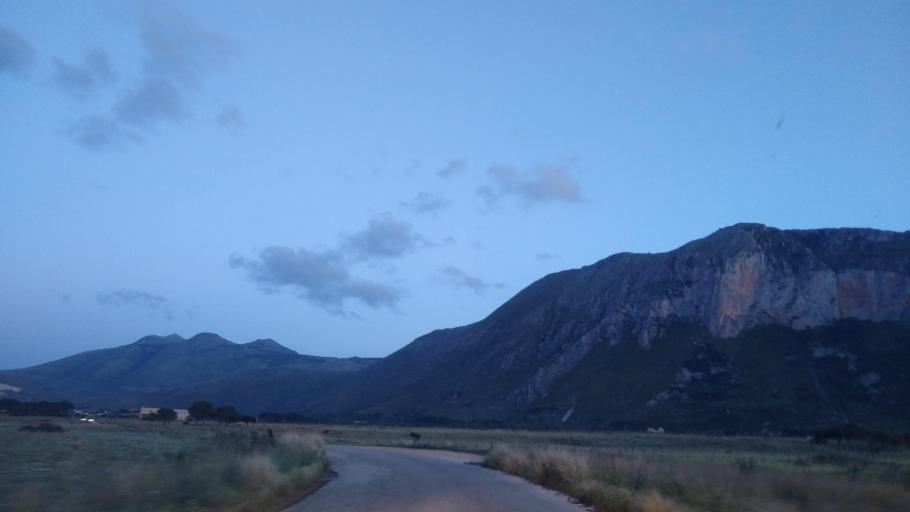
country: IT
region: Sicily
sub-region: Trapani
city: Castelluzzo
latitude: 38.1144
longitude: 12.7202
